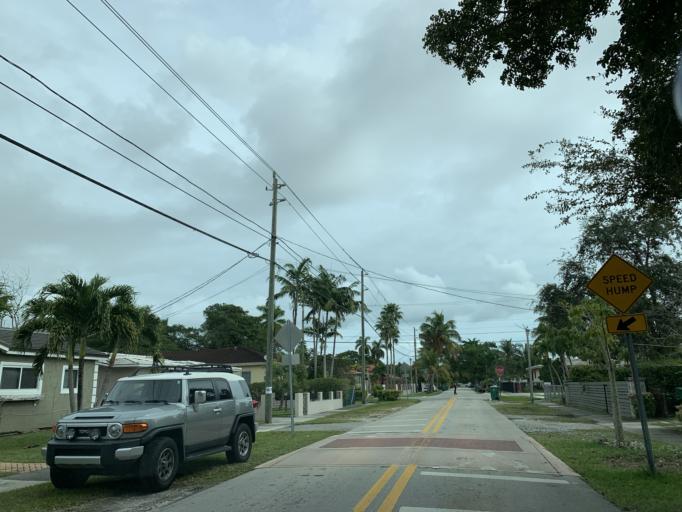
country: US
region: Florida
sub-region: Miami-Dade County
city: Coconut Grove
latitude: 25.7444
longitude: -80.2366
